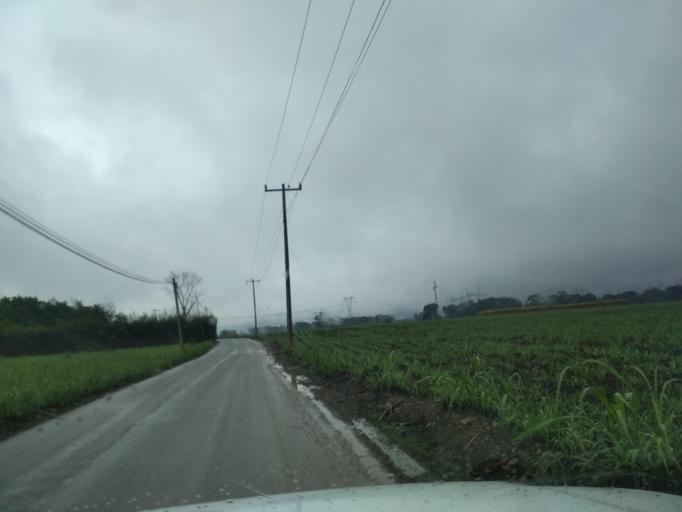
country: MX
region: Veracruz
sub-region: Amatlan de los Reyes
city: Centro de Readaptacion Social
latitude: 18.8311
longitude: -96.9304
